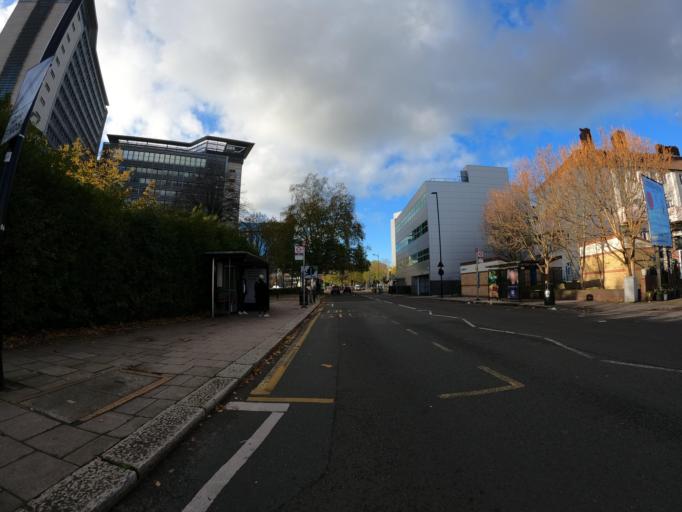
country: GB
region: England
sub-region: Greater London
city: Brentford
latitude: 51.4879
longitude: -0.3119
